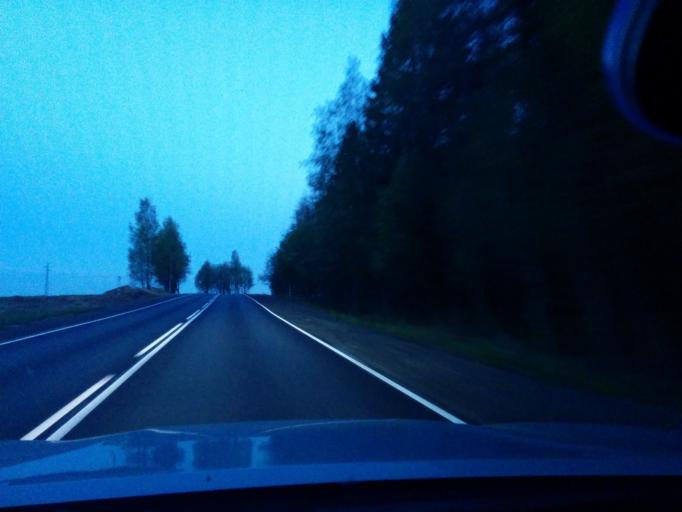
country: RU
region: Leningrad
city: Verkhniye Osel'ki
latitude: 60.1900
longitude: 30.4123
